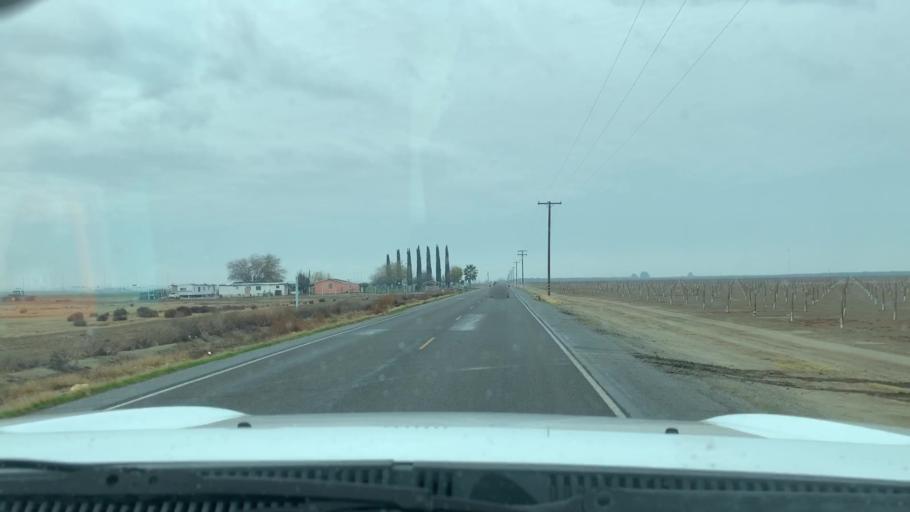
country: US
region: California
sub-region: Kern County
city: Delano
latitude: 35.7612
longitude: -119.3415
